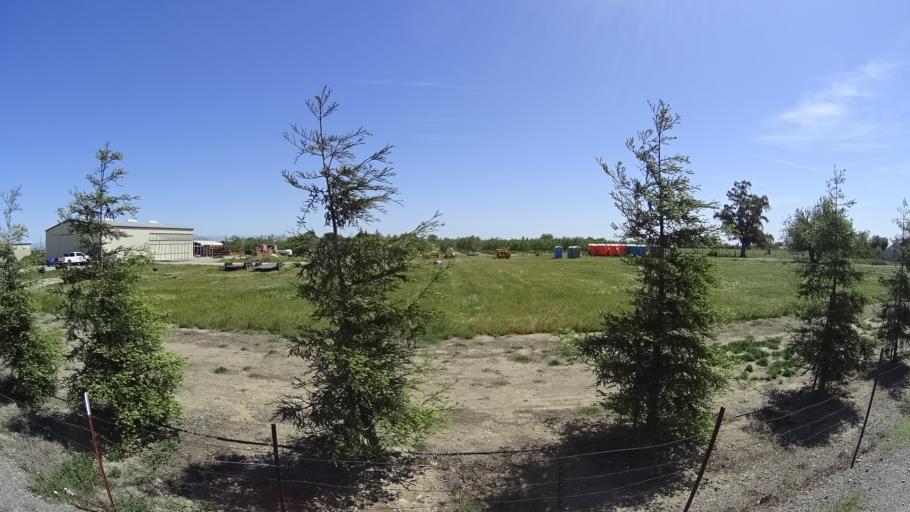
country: US
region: California
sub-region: Glenn County
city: Orland
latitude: 39.7369
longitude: -122.1781
